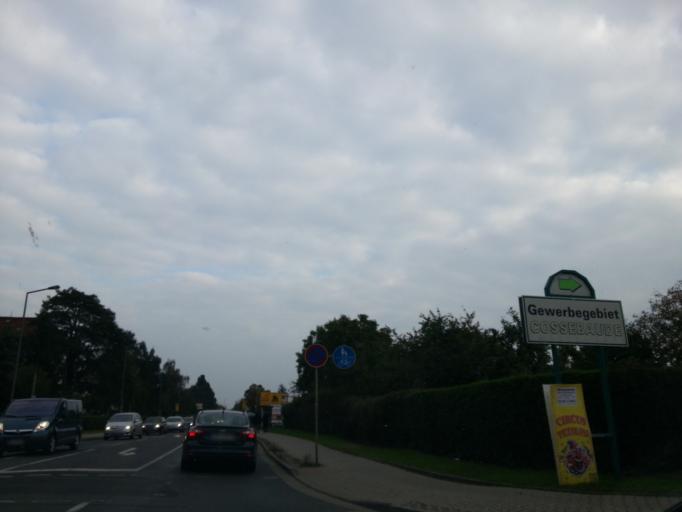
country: DE
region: Saxony
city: Radebeul
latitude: 51.0854
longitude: 13.6447
